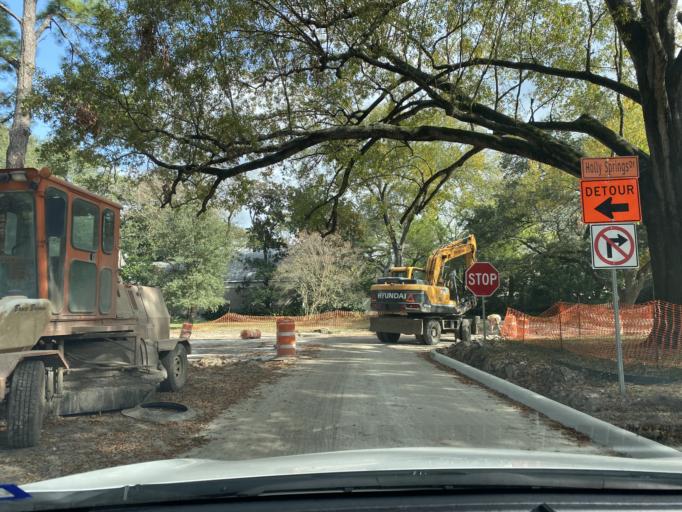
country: US
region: Texas
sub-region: Harris County
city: Hunters Creek Village
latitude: 29.7609
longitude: -95.4713
